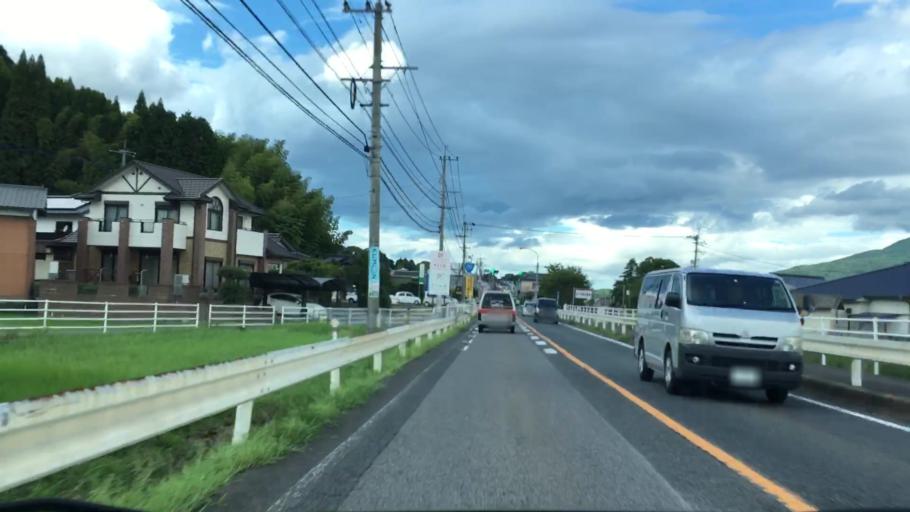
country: JP
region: Saga Prefecture
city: Imaricho-ko
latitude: 33.1996
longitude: 129.8504
